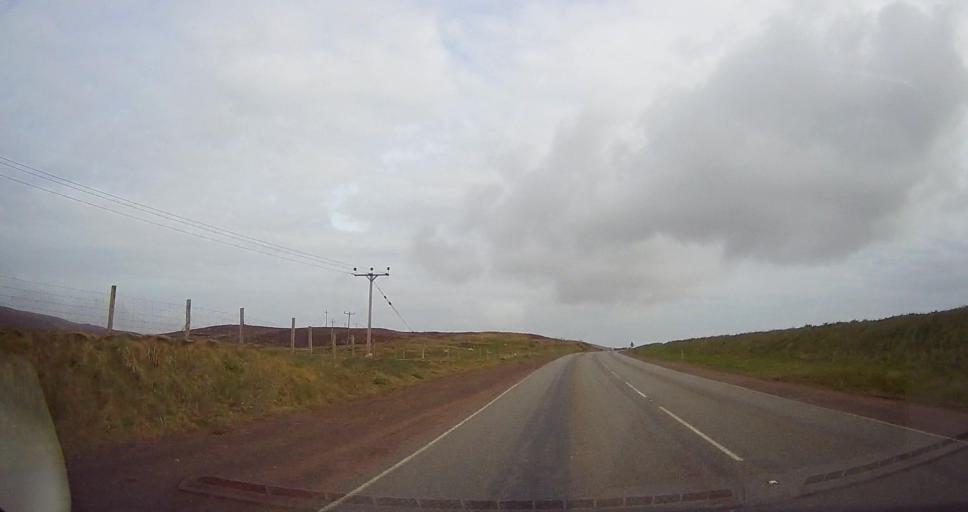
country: GB
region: Scotland
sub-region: Shetland Islands
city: Lerwick
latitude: 60.1143
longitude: -1.2185
